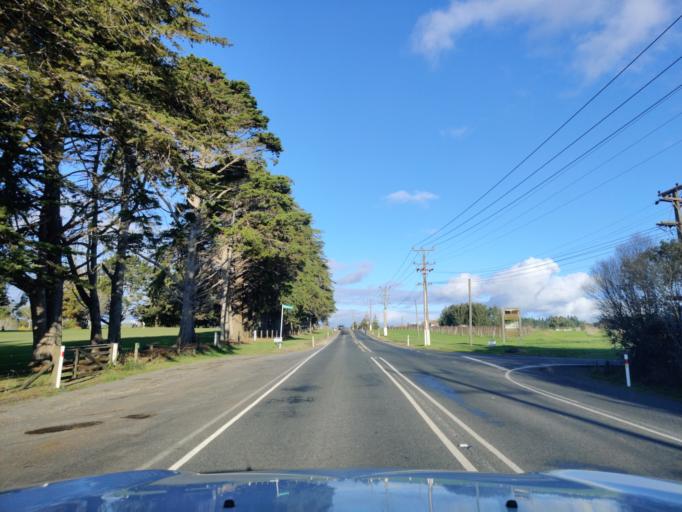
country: NZ
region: Auckland
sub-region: Auckland
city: Pakuranga
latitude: -36.9561
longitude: 174.9696
